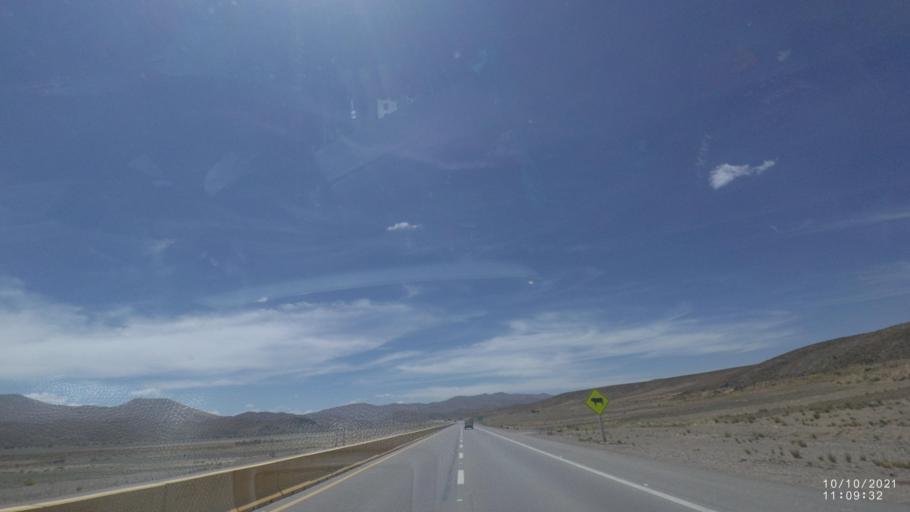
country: BO
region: La Paz
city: Colquiri
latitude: -17.6661
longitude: -67.0439
